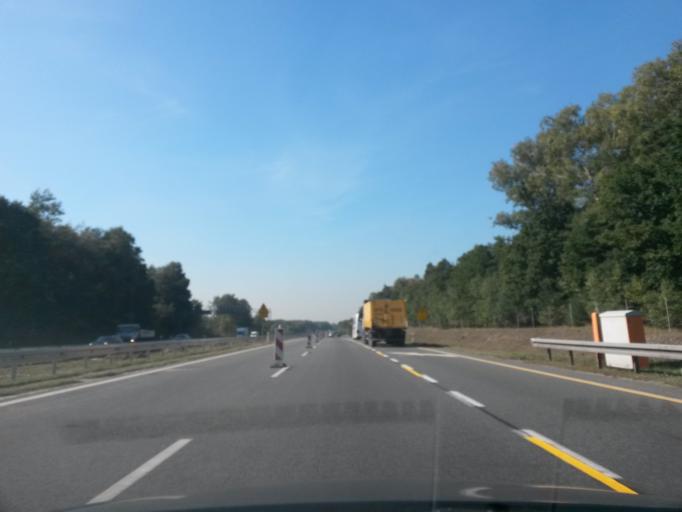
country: PL
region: Silesian Voivodeship
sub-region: Myslowice
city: Myslowice
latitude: 50.2179
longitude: 19.1201
